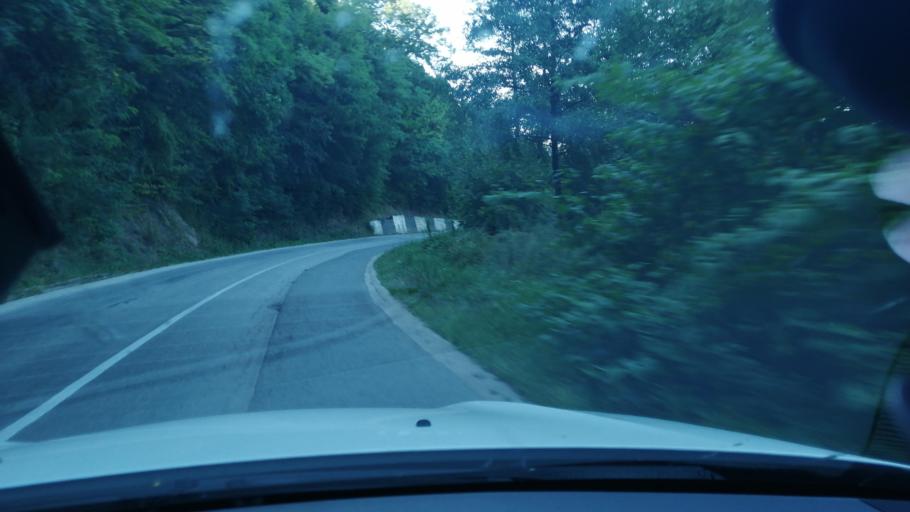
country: RS
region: Central Serbia
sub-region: Zlatiborski Okrug
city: Arilje
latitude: 43.7492
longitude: 20.2547
